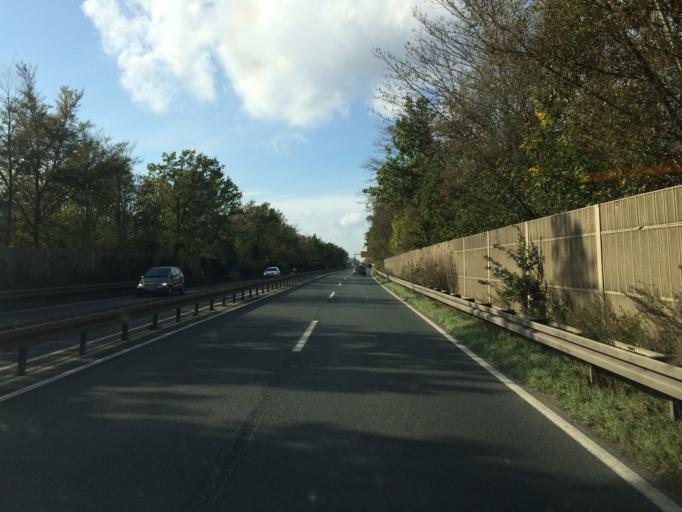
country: DE
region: Lower Saxony
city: Laatzen
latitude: 52.3550
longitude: 9.8415
